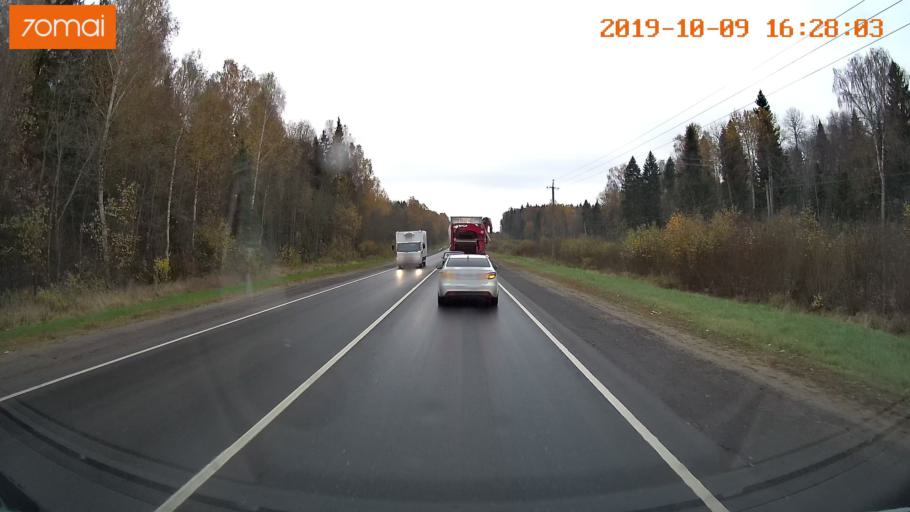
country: RU
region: Kostroma
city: Oktyabr'skiy
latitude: 57.6305
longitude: 40.9305
